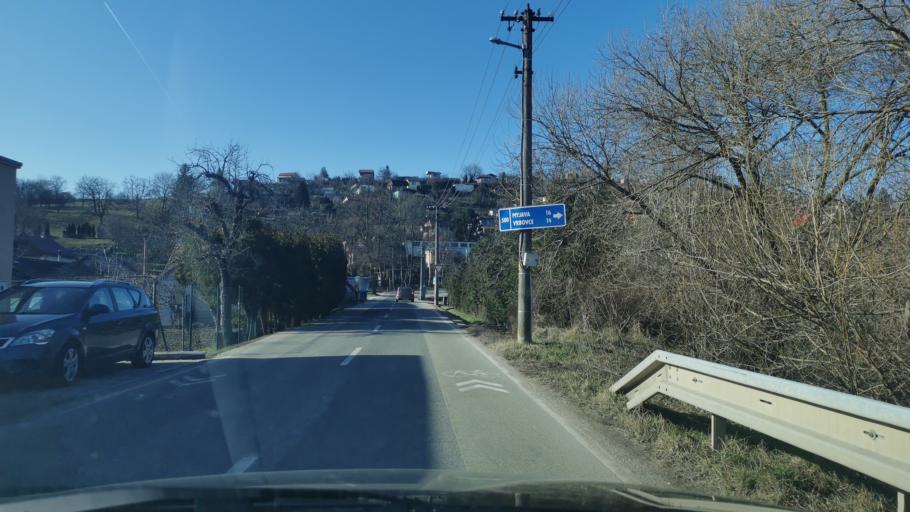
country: SK
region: Trnavsky
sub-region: Okres Senica
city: Senica
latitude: 48.6935
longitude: 17.3994
